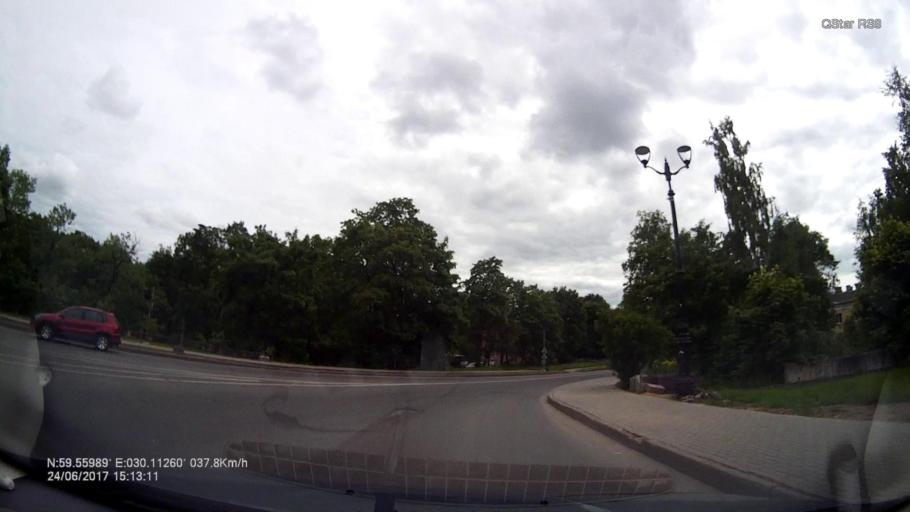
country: RU
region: Leningrad
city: Gatchina
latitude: 59.5600
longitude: 30.1127
